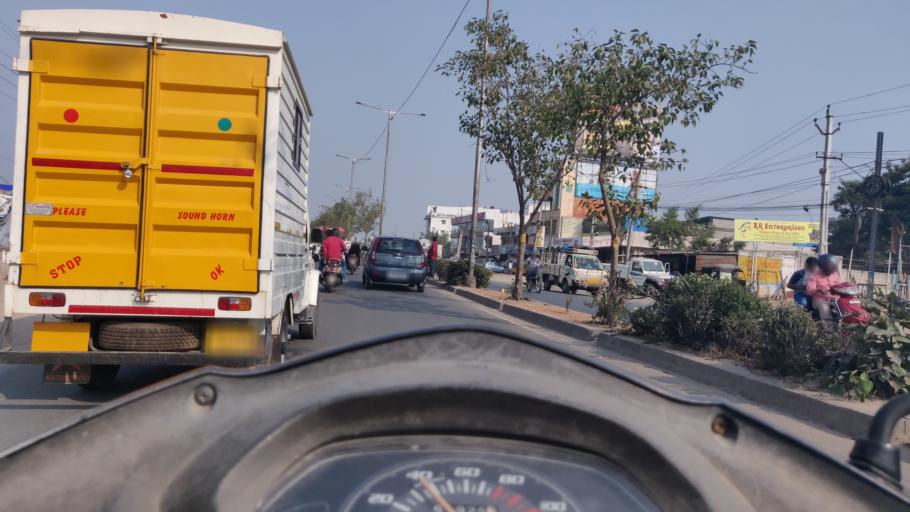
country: IN
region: Telangana
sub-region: Rangareddi
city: Uppal Kalan
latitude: 17.4016
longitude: 78.5732
